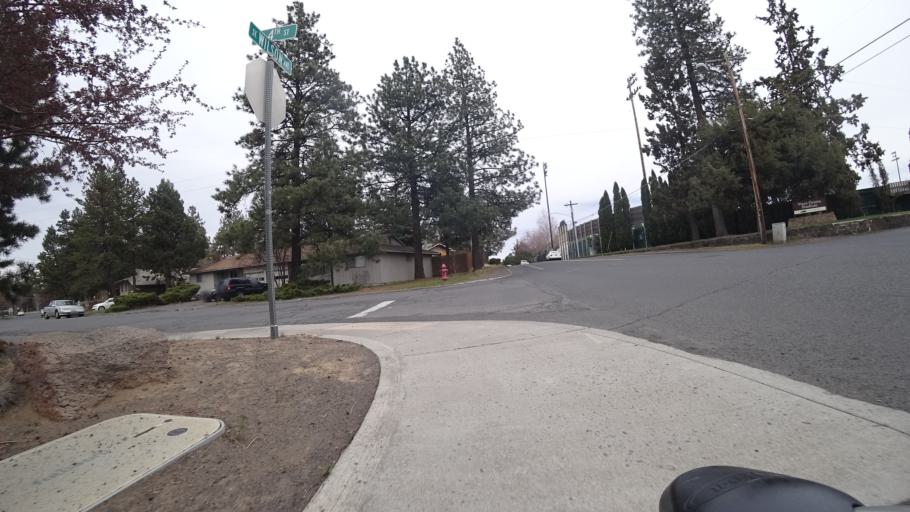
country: US
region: Oregon
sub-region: Deschutes County
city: Bend
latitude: 44.0443
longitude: -121.3009
